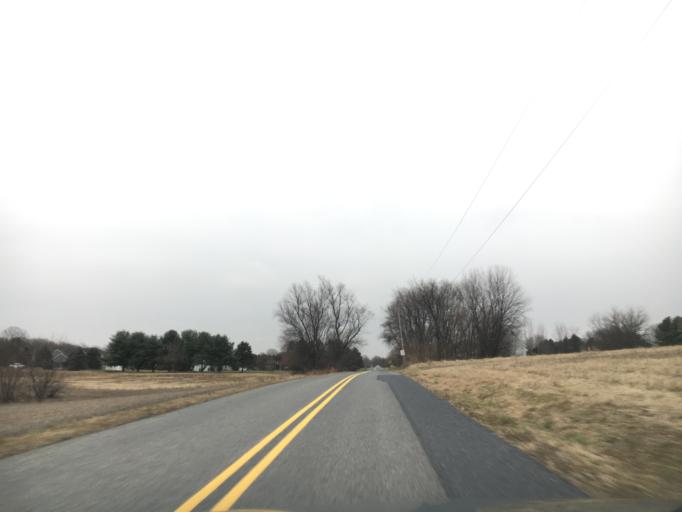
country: US
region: Pennsylvania
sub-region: Lehigh County
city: Schnecksville
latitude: 40.6900
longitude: -75.5837
